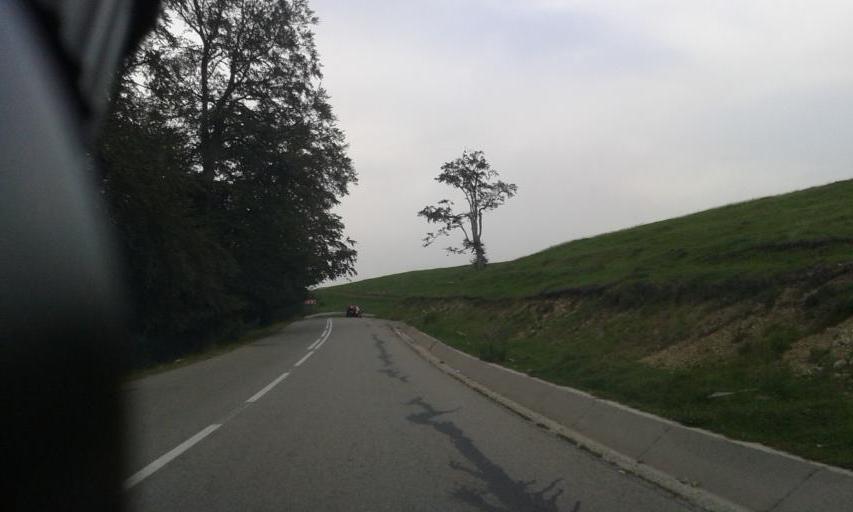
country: RO
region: Gorj
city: Novaci-Straini
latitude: 45.2312
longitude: 23.6873
